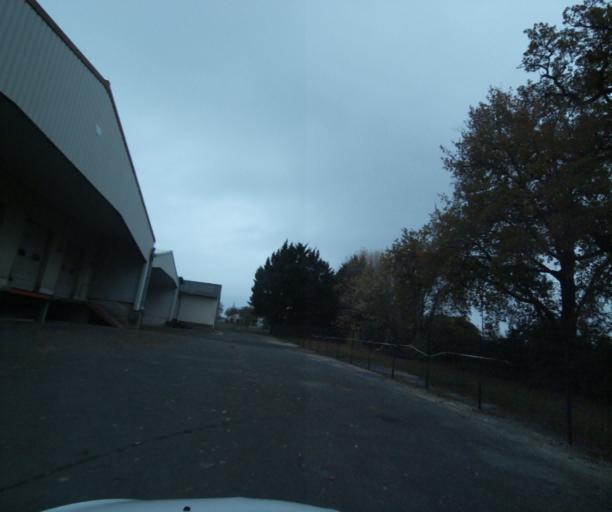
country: FR
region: Poitou-Charentes
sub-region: Departement de la Charente-Maritime
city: Fontcouverte
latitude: 45.7459
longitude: -0.5979
